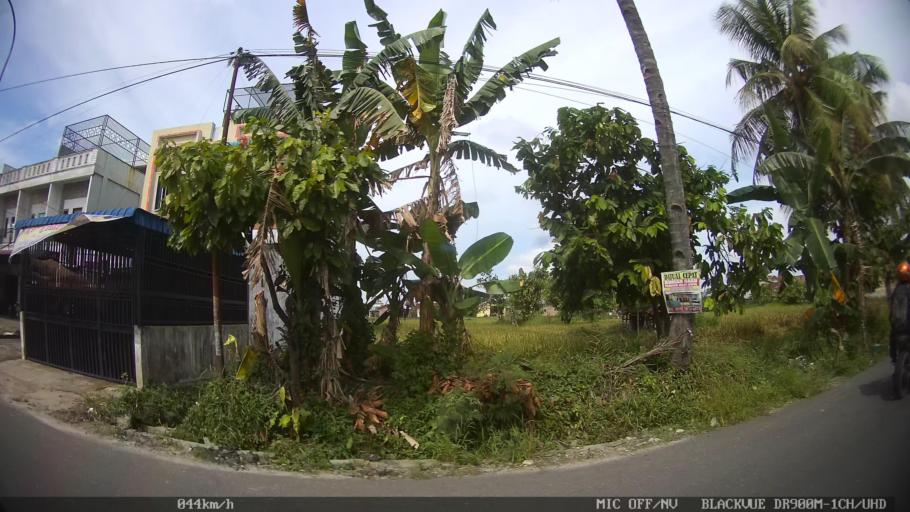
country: ID
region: North Sumatra
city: Percut
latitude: 3.5801
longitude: 98.8637
